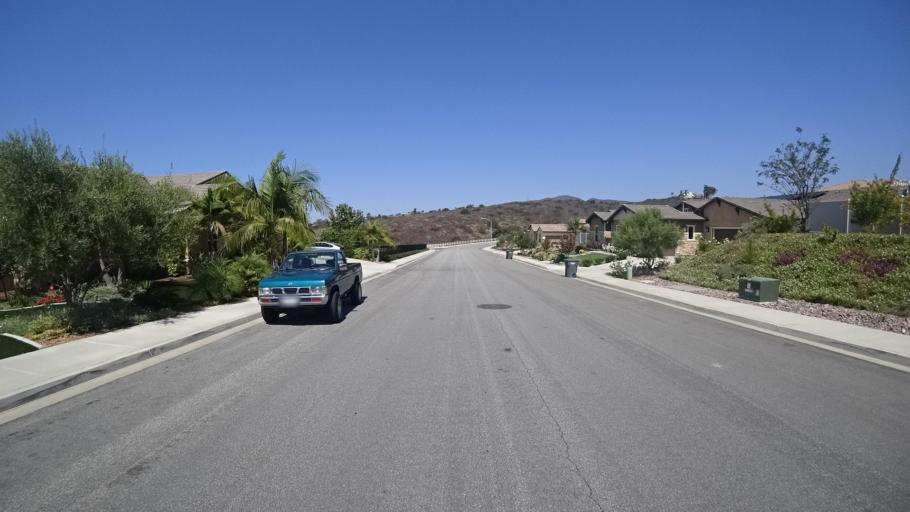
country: US
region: California
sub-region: San Diego County
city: San Marcos
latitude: 33.1828
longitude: -117.1950
